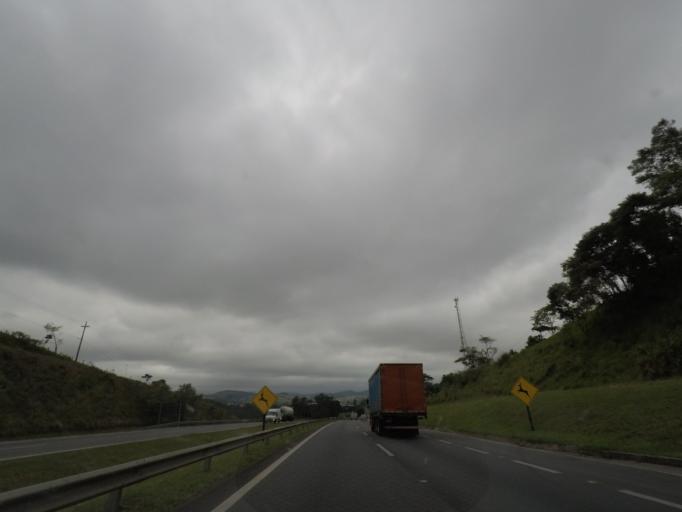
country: BR
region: Sao Paulo
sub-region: Bom Jesus Dos Perdoes
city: Bom Jesus dos Perdoes
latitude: -23.1095
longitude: -46.4971
